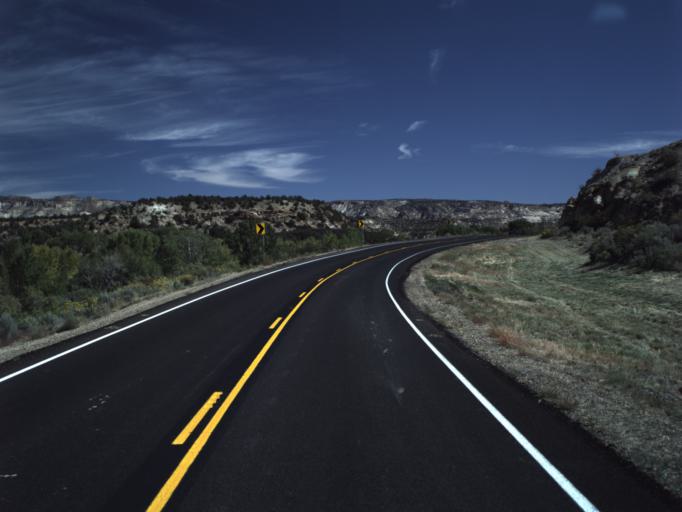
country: US
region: Utah
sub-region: Wayne County
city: Loa
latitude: 37.7718
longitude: -111.6596
